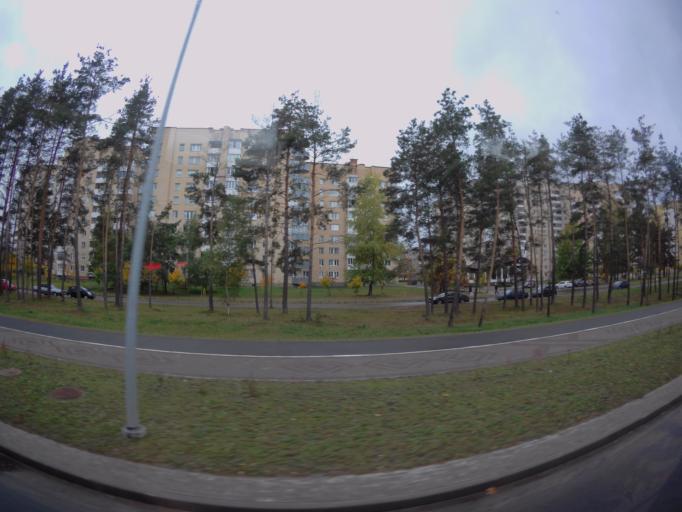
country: BY
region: Minsk
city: Horad Barysaw
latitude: 54.2055
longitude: 28.4838
